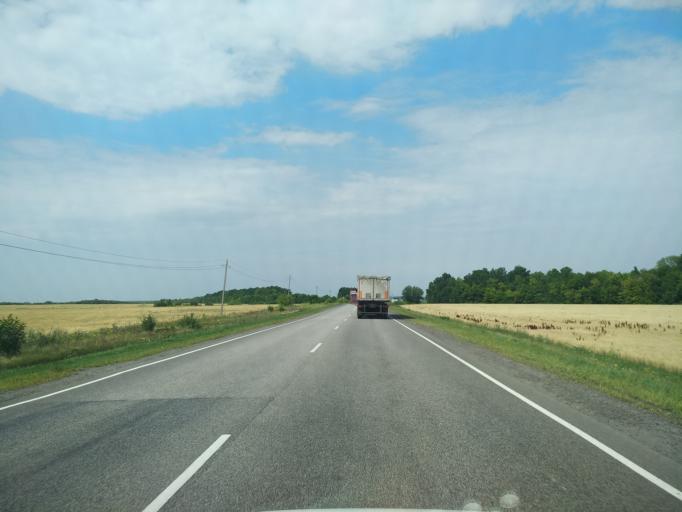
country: RU
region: Voronezj
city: Orlovo
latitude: 51.6762
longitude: 39.7696
